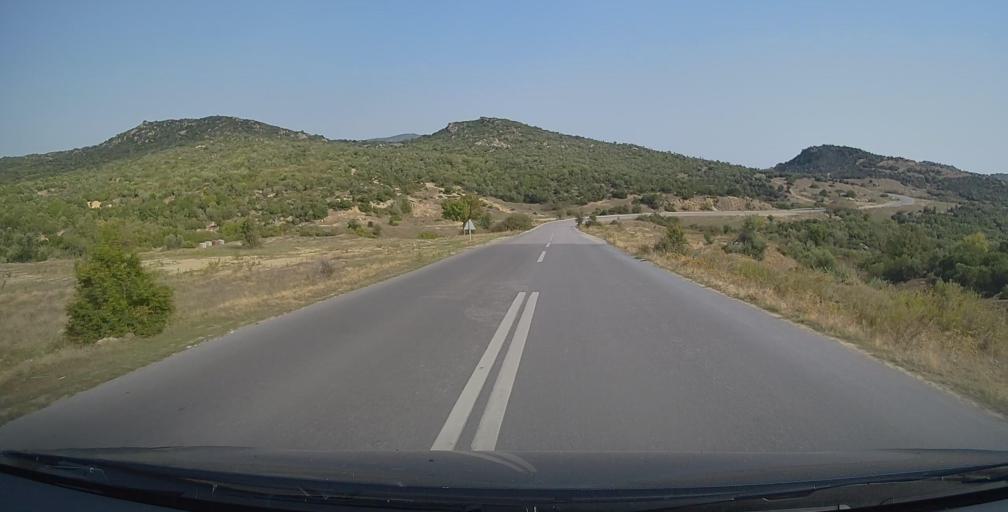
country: GR
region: Central Macedonia
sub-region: Nomos Chalkidikis
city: Sykia
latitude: 40.0201
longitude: 23.9864
